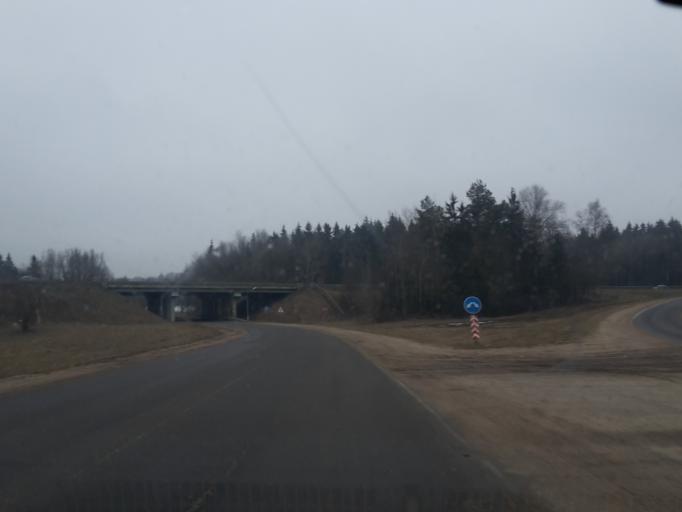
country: BY
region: Minsk
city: Zhdanovichy
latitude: 53.9116
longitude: 27.3914
